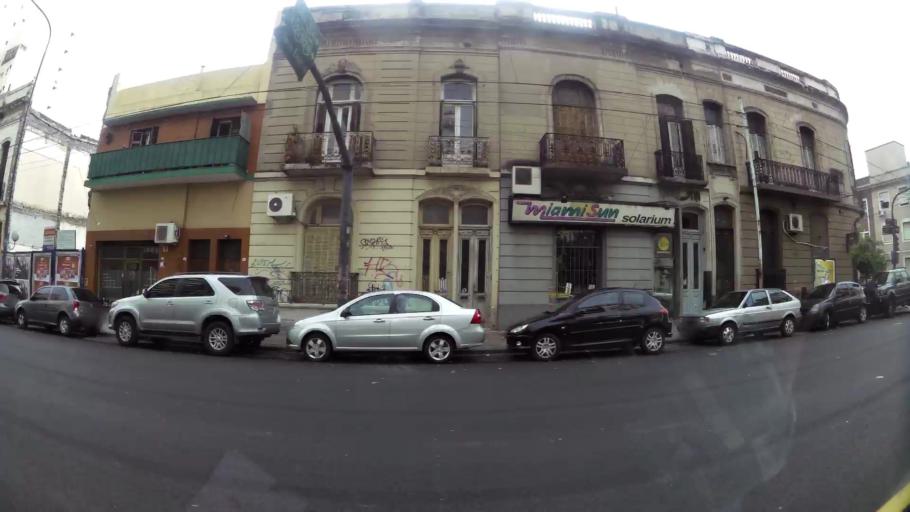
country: AR
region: Buenos Aires F.D.
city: Villa Santa Rita
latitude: -34.6323
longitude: -58.4689
